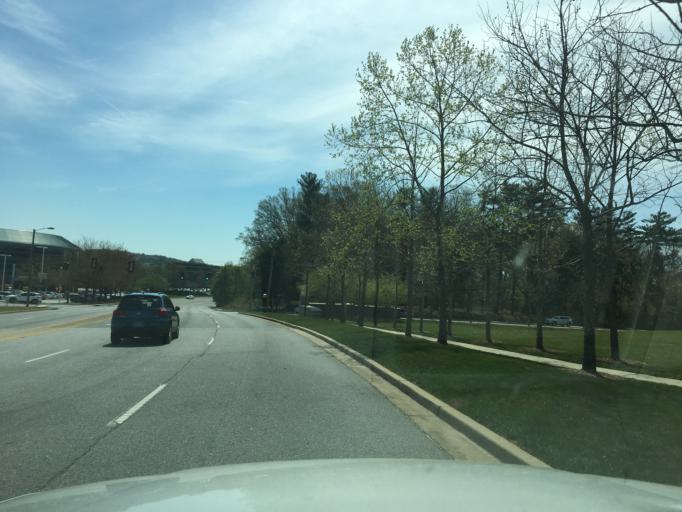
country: US
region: South Carolina
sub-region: Greenville County
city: Wade Hampton
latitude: 34.8524
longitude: -82.3260
